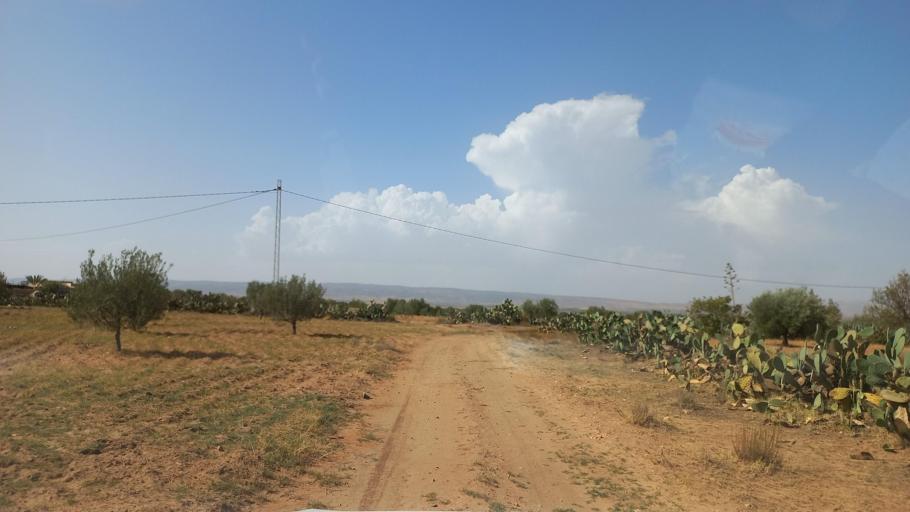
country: TN
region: Al Qasrayn
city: Kasserine
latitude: 35.2039
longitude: 9.0196
